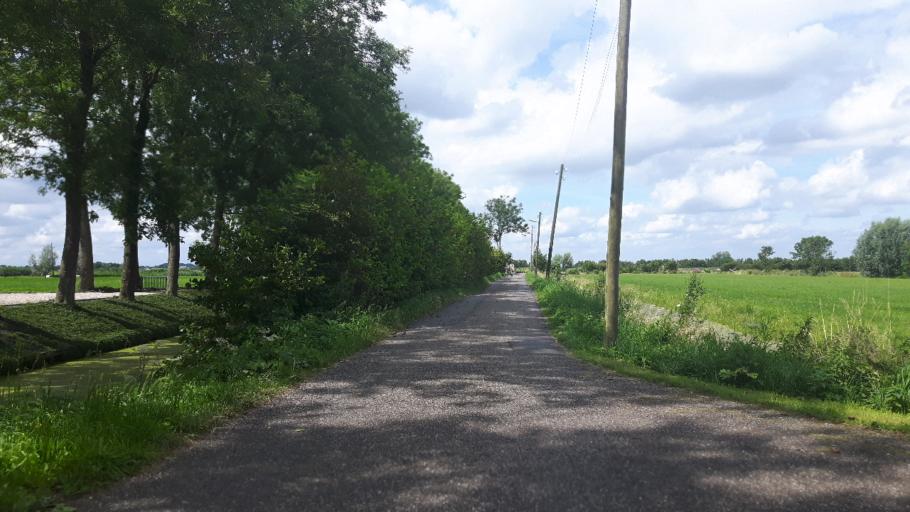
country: NL
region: South Holland
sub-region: Gemeente Vlist
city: Vlist
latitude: 51.9642
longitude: 4.8070
